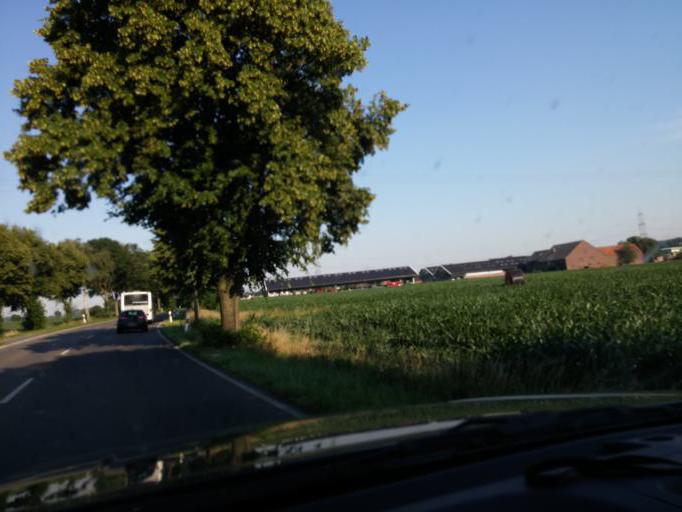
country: DE
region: North Rhine-Westphalia
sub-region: Regierungsbezirk Dusseldorf
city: Viersen
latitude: 51.2628
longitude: 6.4557
